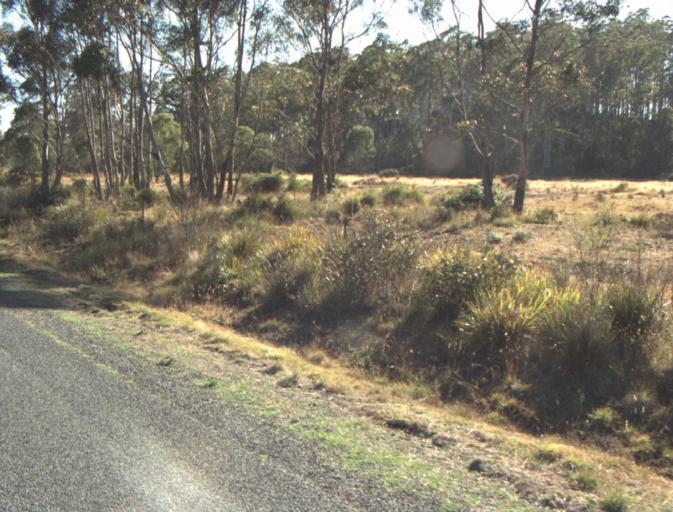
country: AU
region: Tasmania
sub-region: Launceston
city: Newstead
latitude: -41.3725
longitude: 147.2977
